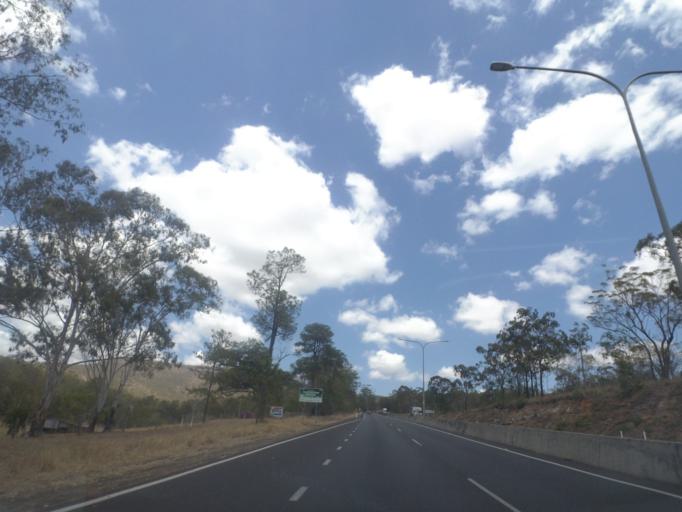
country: AU
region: Queensland
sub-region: Toowoomba
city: East Toowoomba
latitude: -27.5636
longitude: 152.0024
